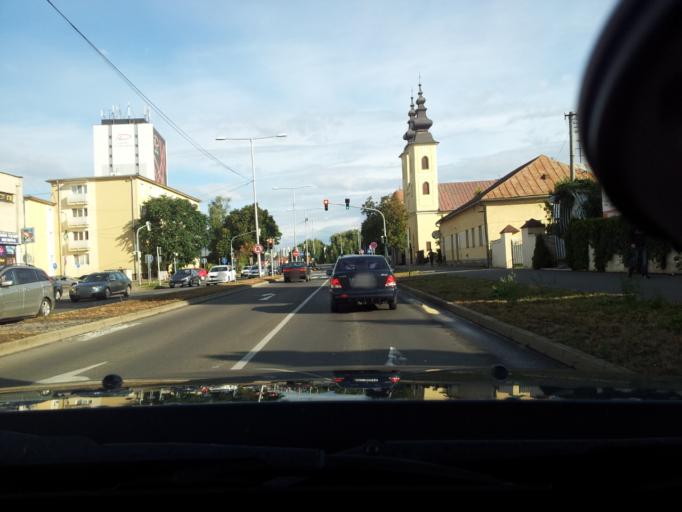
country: SK
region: Kosicky
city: Michalovce
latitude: 48.7556
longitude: 21.9240
